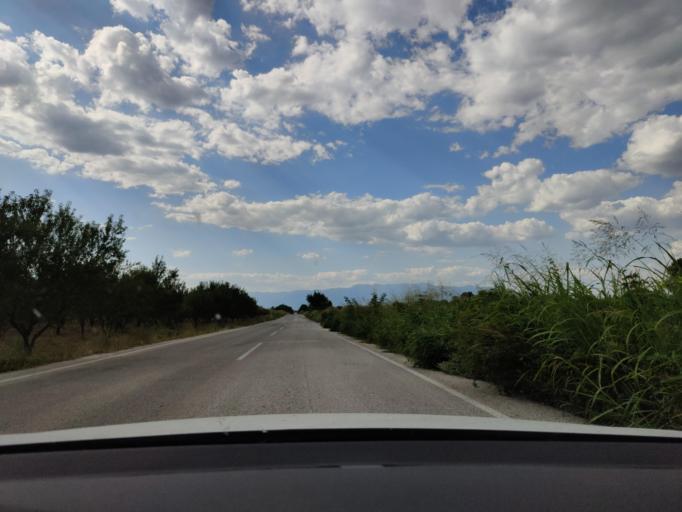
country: GR
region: Central Macedonia
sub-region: Nomos Serron
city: Strymoniko
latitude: 41.0646
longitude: 23.3073
